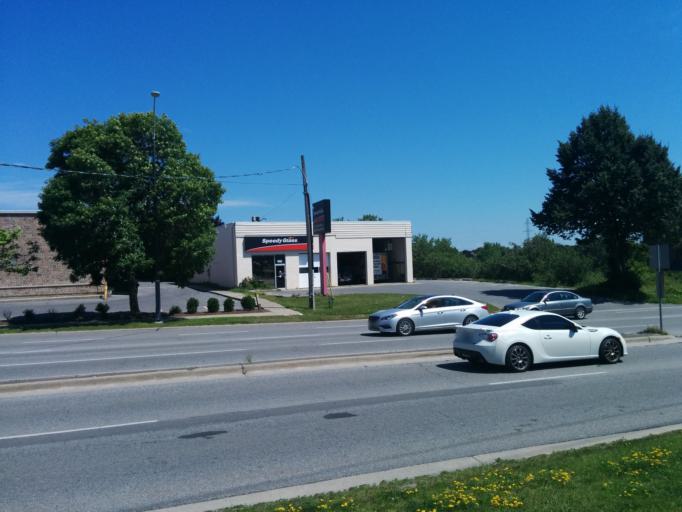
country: CA
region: Ontario
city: Kingston
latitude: 44.2574
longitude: -76.5692
